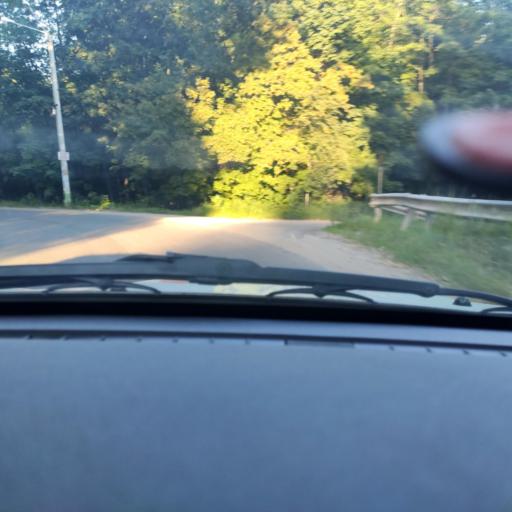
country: RU
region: Voronezj
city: Ramon'
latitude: 51.8937
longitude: 39.2810
